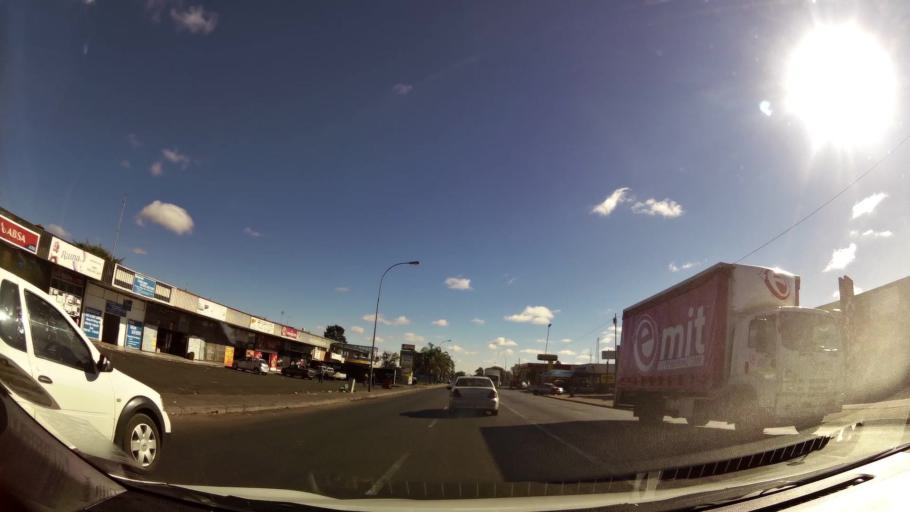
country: ZA
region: Limpopo
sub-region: Capricorn District Municipality
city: Polokwane
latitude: -23.8791
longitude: 29.4418
